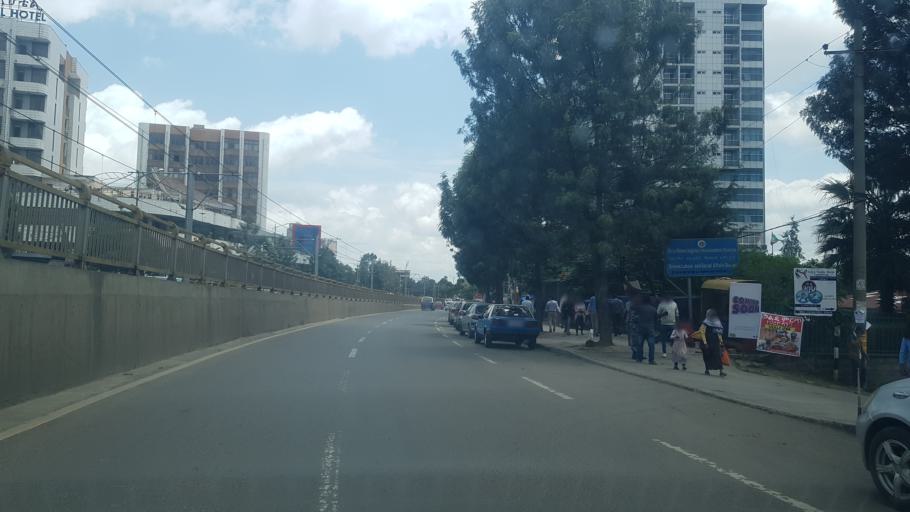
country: ET
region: Adis Abeba
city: Addis Ababa
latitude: 8.9946
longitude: 38.7597
